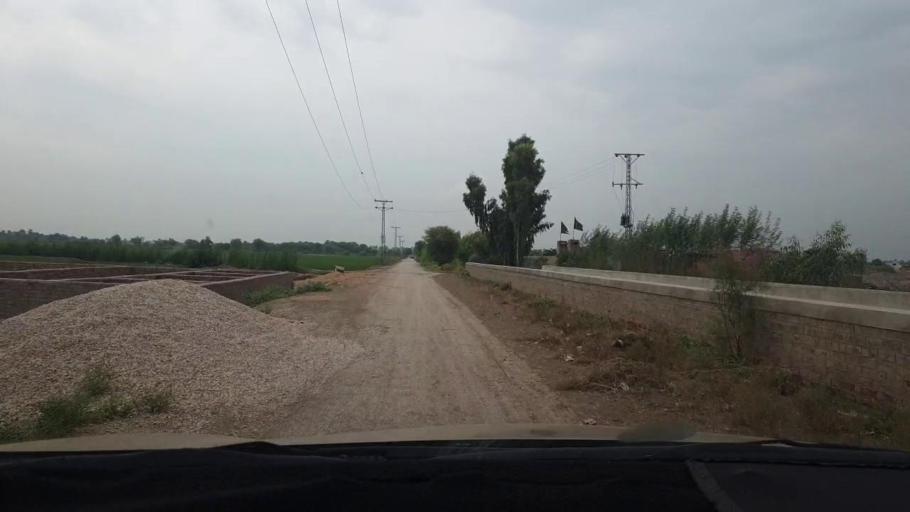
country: PK
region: Sindh
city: Larkana
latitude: 27.5802
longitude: 68.2350
